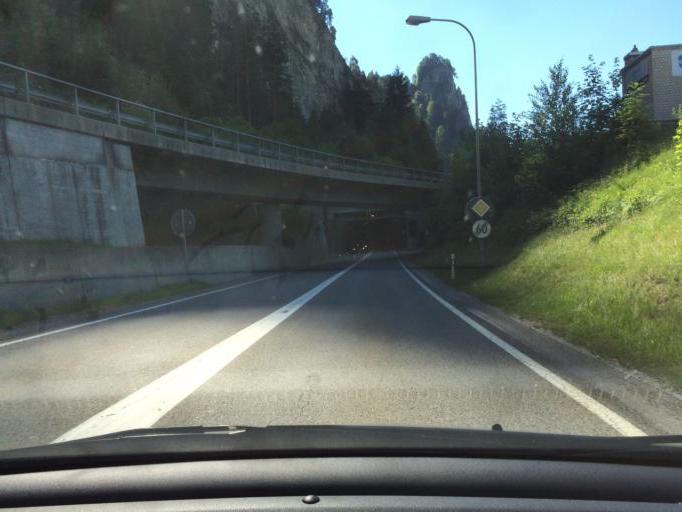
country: CH
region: Grisons
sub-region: Imboden District
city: Bonaduz
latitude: 46.8334
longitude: 9.3444
